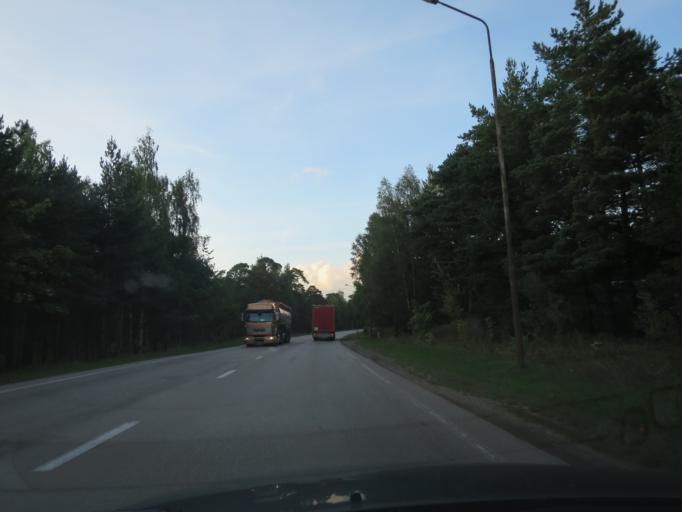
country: LV
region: Salacgrivas
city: Salacgriva
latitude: 57.7626
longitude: 24.3569
